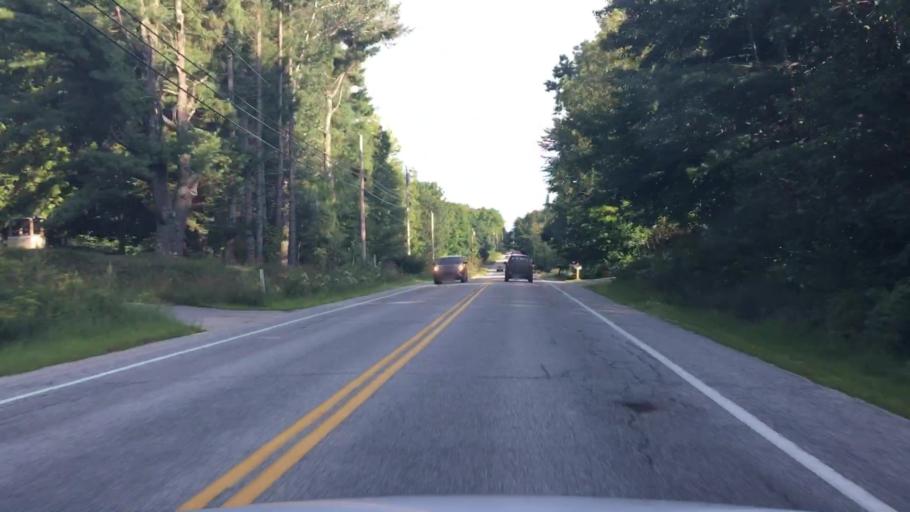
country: US
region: Maine
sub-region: Cumberland County
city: South Windham
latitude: 43.7430
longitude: -70.4230
